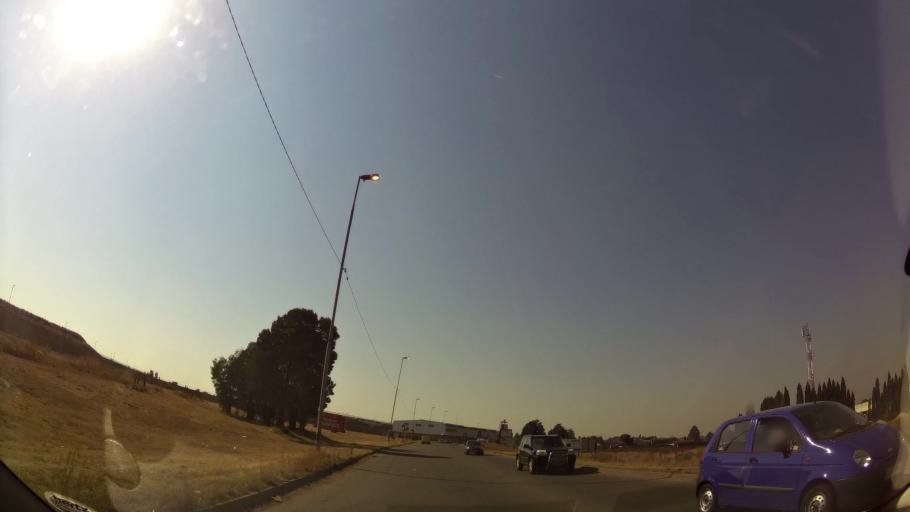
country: ZA
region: Gauteng
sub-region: Ekurhuleni Metropolitan Municipality
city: Boksburg
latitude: -26.1685
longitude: 28.2490
